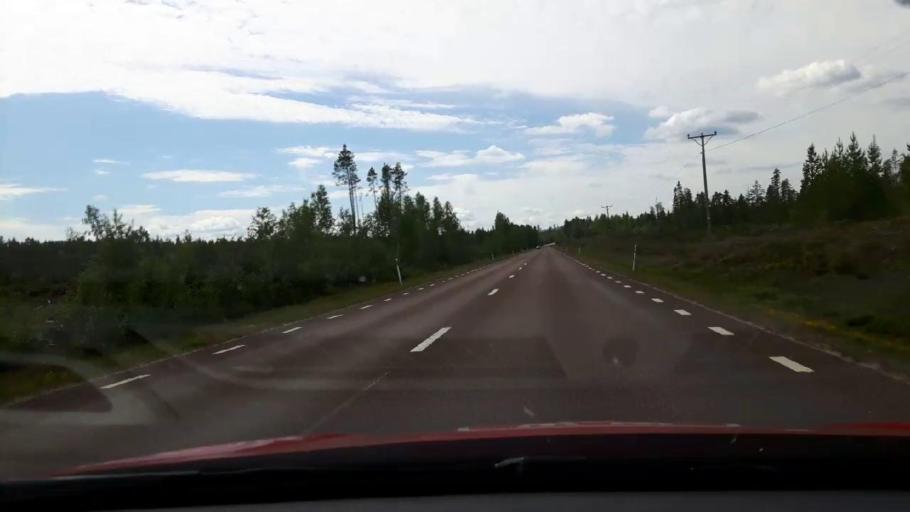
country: SE
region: Jaemtland
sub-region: Harjedalens Kommun
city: Sveg
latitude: 62.0586
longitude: 14.9091
